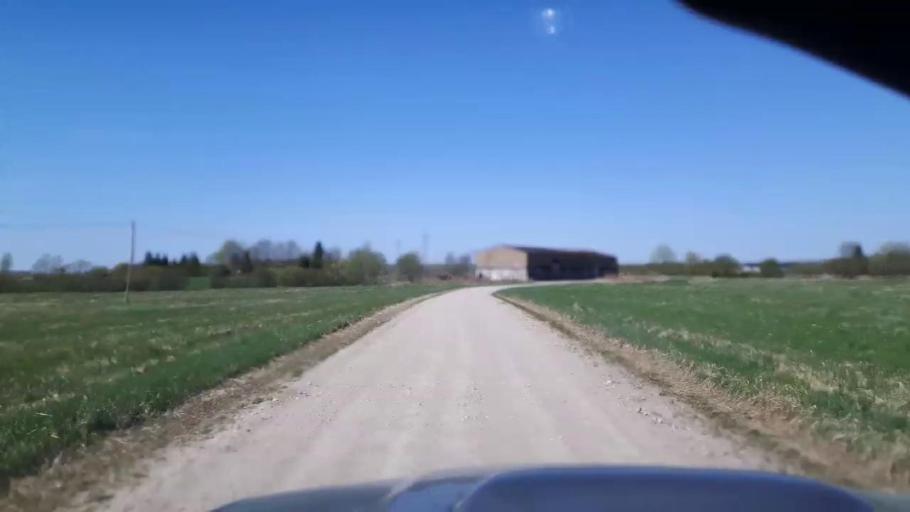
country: EE
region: Paernumaa
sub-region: Sindi linn
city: Sindi
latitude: 58.4454
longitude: 24.7781
